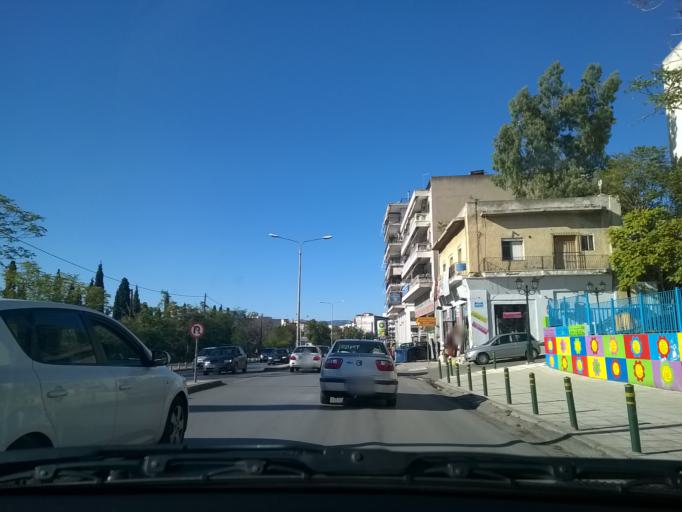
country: GR
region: Central Macedonia
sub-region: Nomos Thessalonikis
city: Ampelokipoi
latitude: 40.6547
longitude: 22.9348
